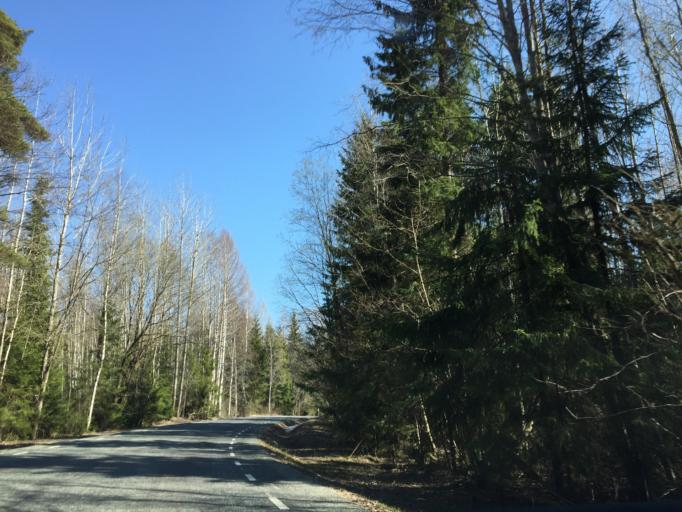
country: EE
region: Tartu
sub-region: Alatskivi vald
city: Kallaste
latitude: 58.5945
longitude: 27.0702
